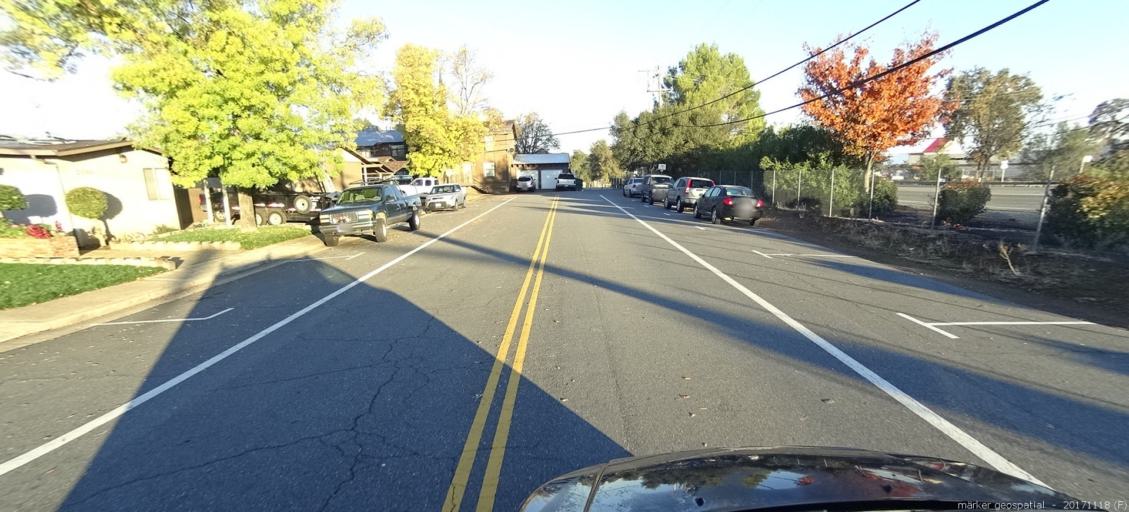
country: US
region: California
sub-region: Shasta County
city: Anderson
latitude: 40.4388
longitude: -122.2919
